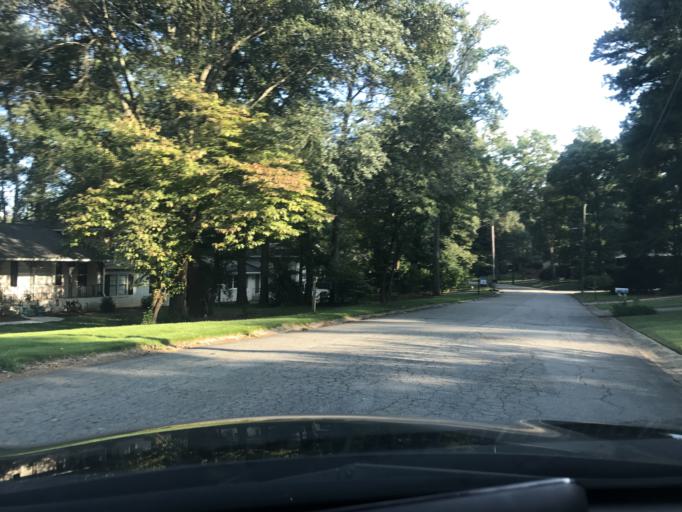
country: US
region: Georgia
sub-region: DeKalb County
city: North Druid Hills
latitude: 33.8262
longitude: -84.2778
